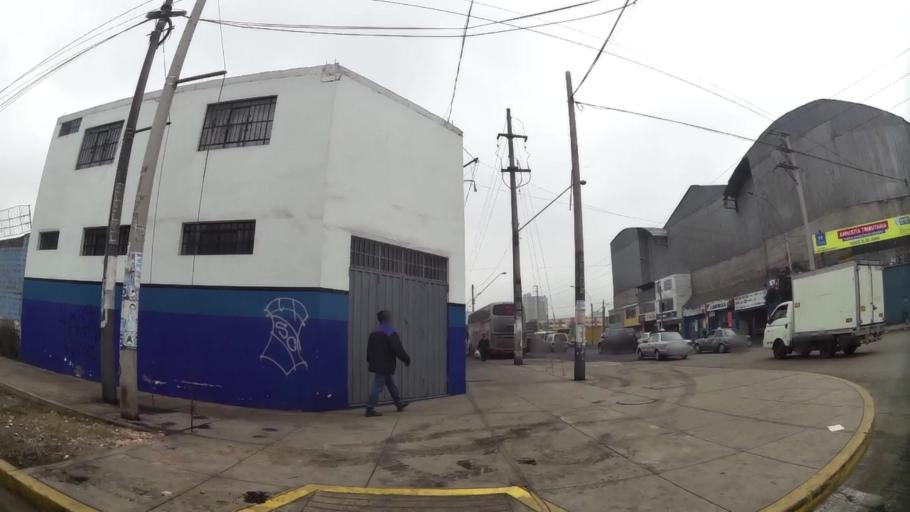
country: PE
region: Lima
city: Lima
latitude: -12.0637
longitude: -77.0227
